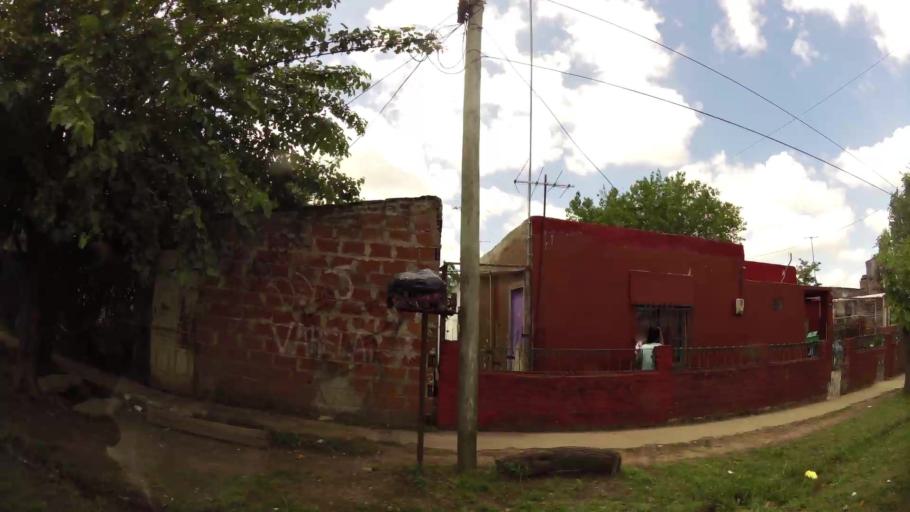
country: AR
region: Buenos Aires
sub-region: Partido de Quilmes
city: Quilmes
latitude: -34.8246
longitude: -58.2447
